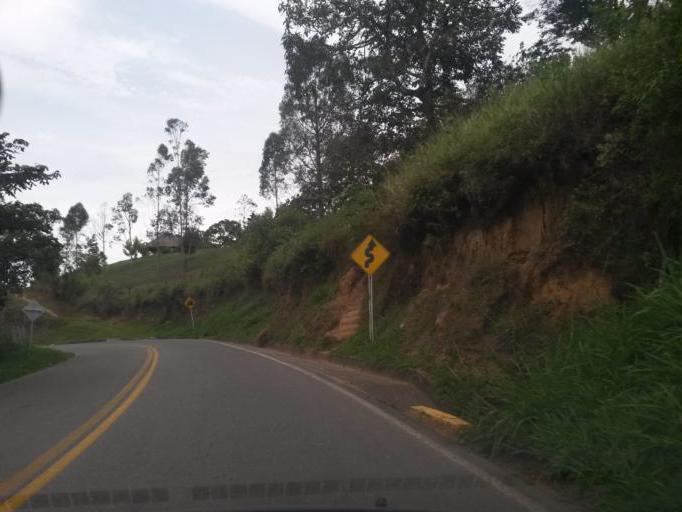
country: CO
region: Cauca
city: Lopez
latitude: 2.4339
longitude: -76.7569
